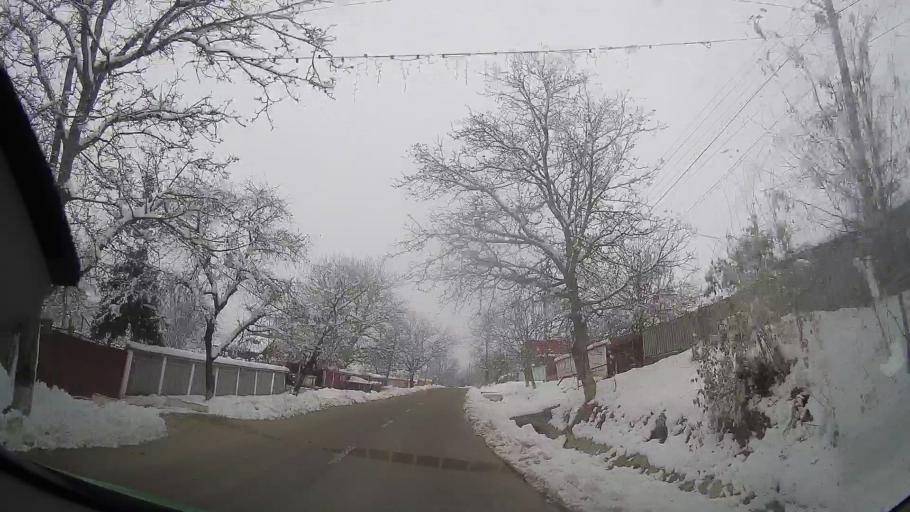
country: RO
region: Neamt
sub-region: Comuna Bozieni
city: Bozieni
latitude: 46.8387
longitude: 27.1503
